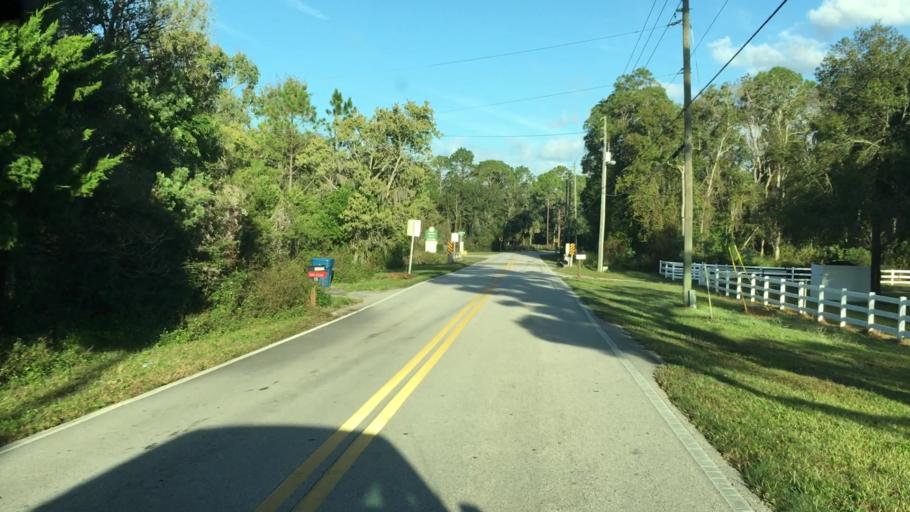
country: US
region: Florida
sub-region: Volusia County
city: North DeLand
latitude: 29.0752
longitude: -81.2727
